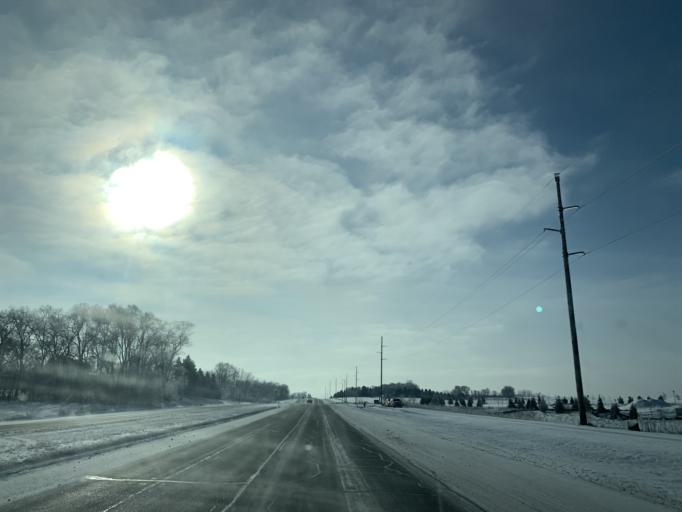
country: US
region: Minnesota
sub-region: Dakota County
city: Lakeville
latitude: 44.6835
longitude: -93.2174
